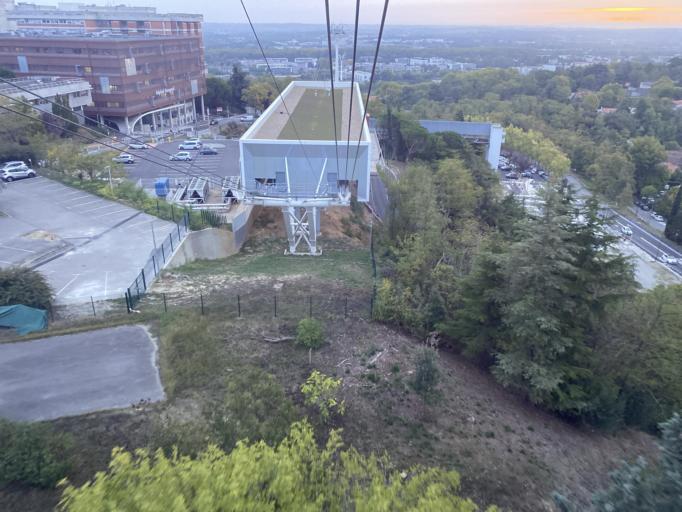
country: FR
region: Midi-Pyrenees
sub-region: Departement de la Haute-Garonne
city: Ramonville-Saint-Agne
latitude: 43.5581
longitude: 1.4518
